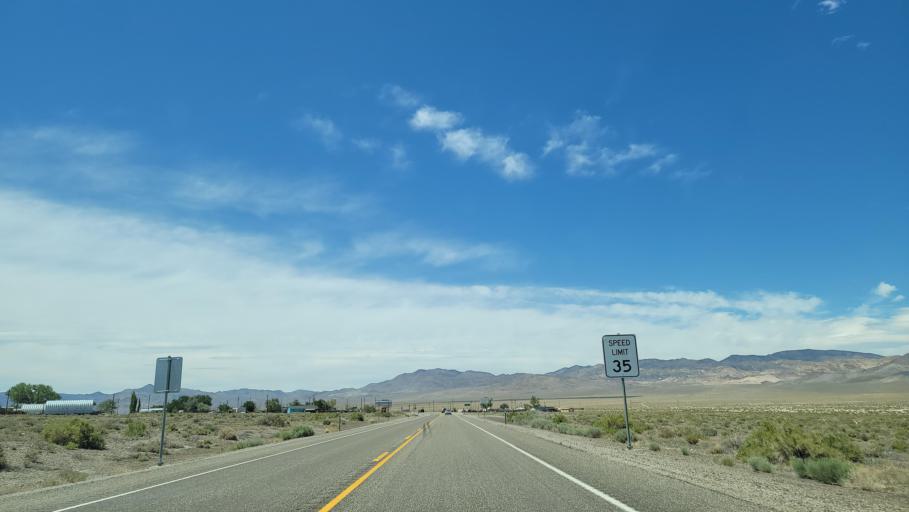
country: US
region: Nevada
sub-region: Mineral County
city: Hawthorne
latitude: 38.5011
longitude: -118.1747
